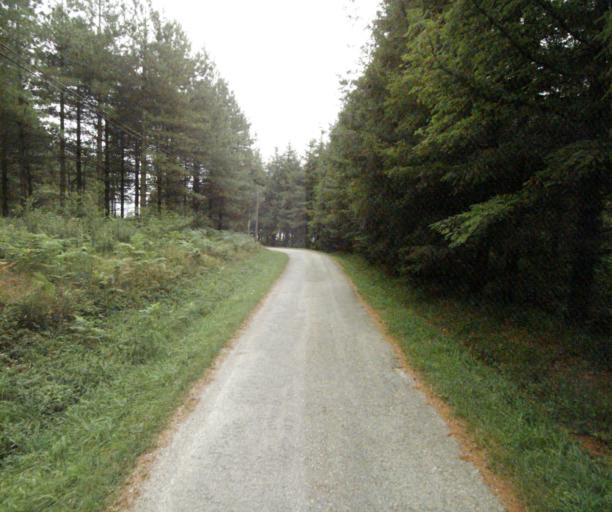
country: FR
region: Midi-Pyrenees
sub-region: Departement du Tarn
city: Soreze
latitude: 43.4180
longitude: 2.0474
